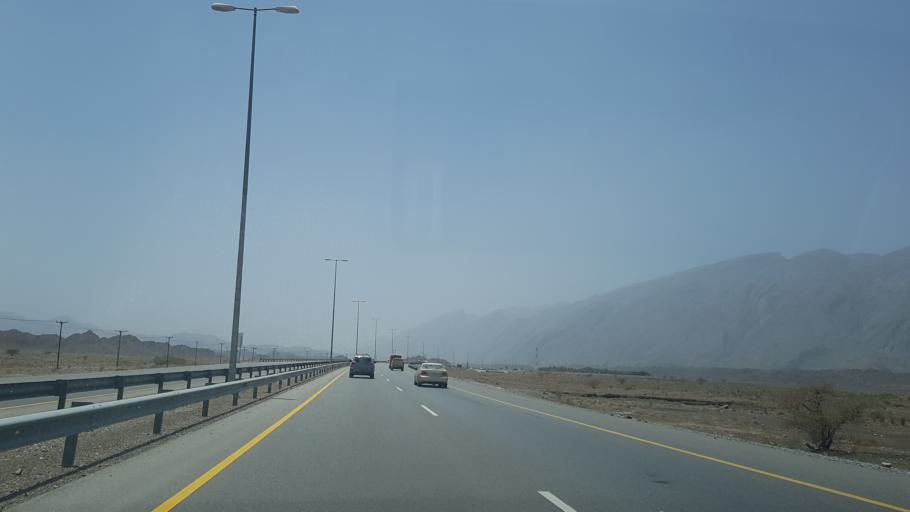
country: OM
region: Muhafazat ad Dakhiliyah
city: Sufalat Sama'il
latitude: 23.2562
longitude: 57.9291
